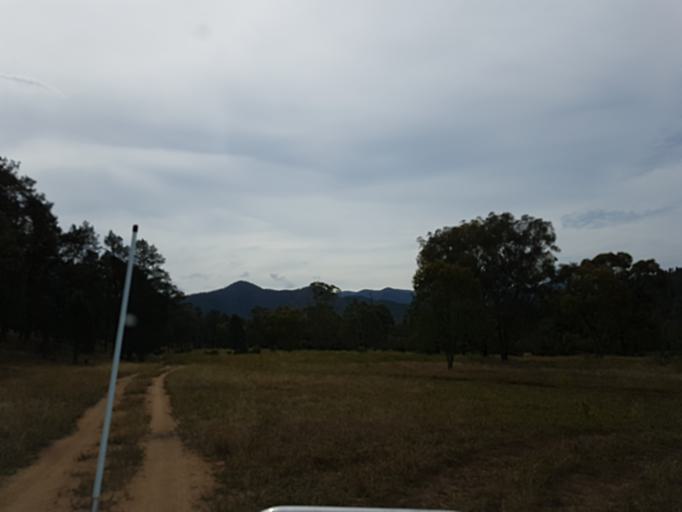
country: AU
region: New South Wales
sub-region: Snowy River
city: Jindabyne
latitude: -36.9531
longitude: 148.4056
